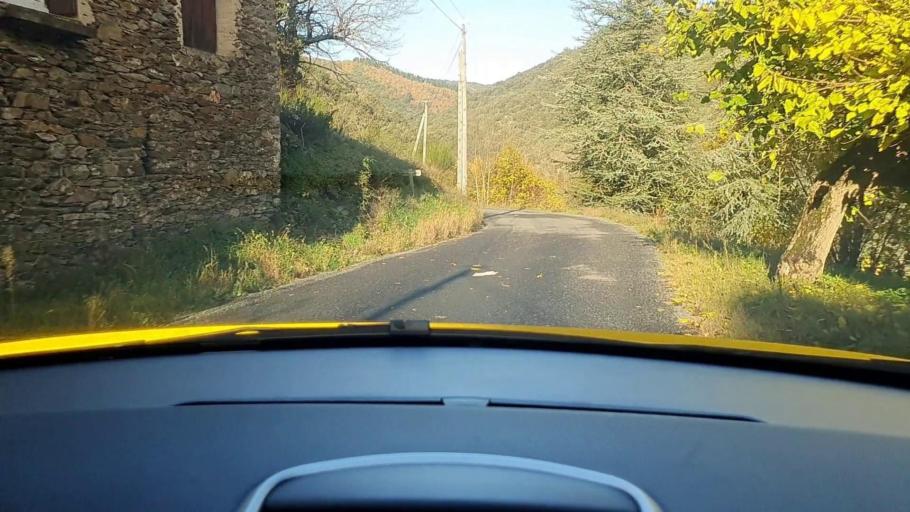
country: FR
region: Languedoc-Roussillon
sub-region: Departement du Gard
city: Valleraugue
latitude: 44.1042
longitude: 3.7313
